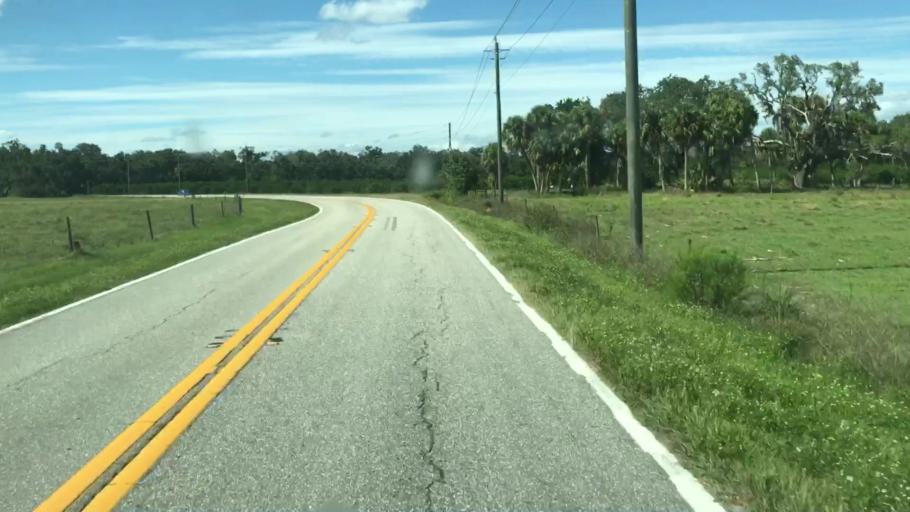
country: US
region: Florida
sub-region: Lee County
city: Alva
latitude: 26.7253
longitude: -81.6211
